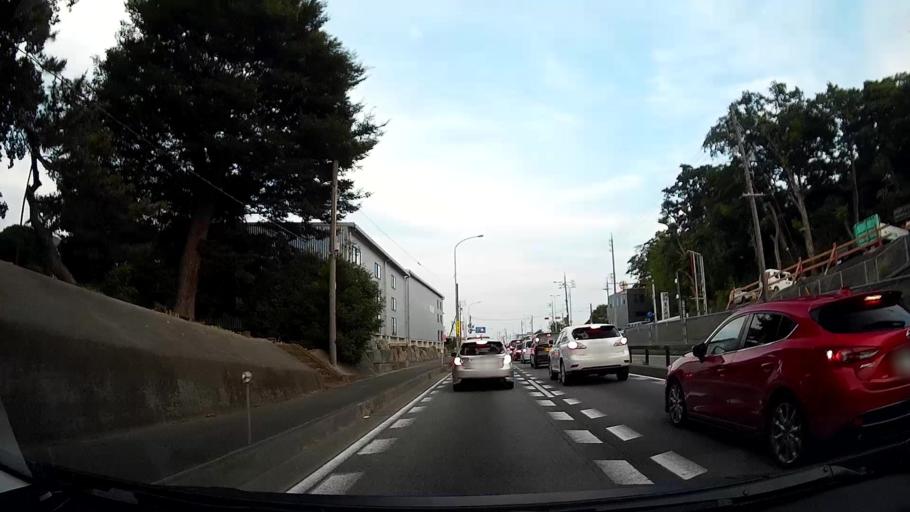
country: JP
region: Aichi
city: Kozakai-cho
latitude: 34.7982
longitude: 137.3663
